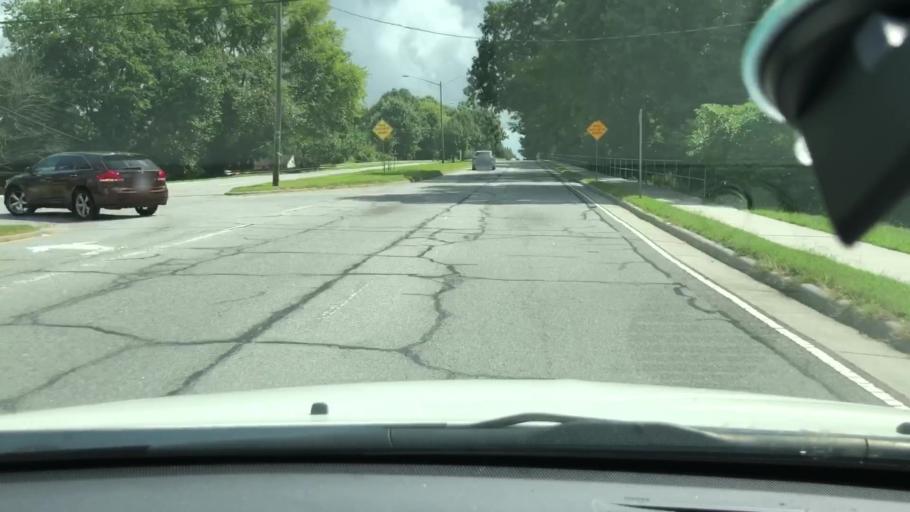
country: US
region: Virginia
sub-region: City of Chesapeake
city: Chesapeake
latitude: 36.8130
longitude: -76.1980
